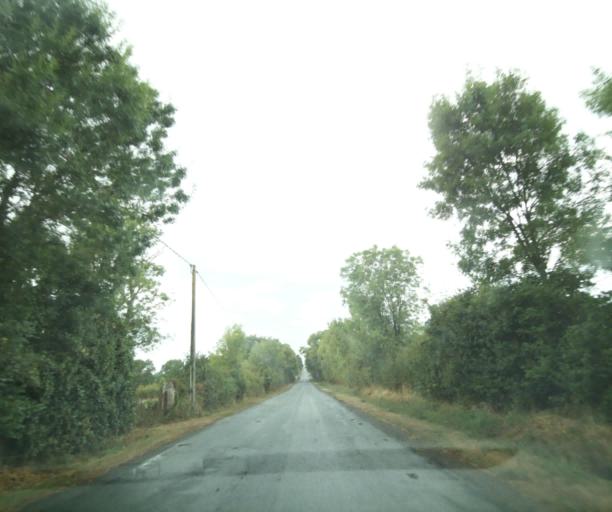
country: FR
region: Poitou-Charentes
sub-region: Departement de la Charente-Maritime
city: Tonnay-Charente
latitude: 45.9416
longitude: -0.8752
